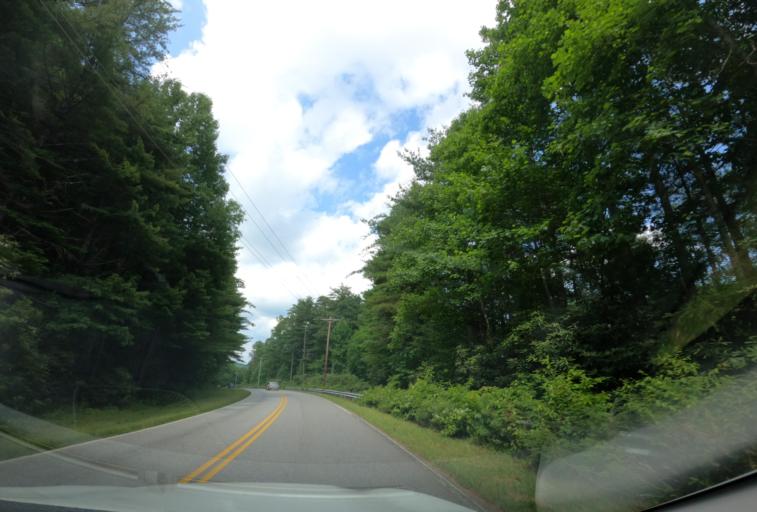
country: US
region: North Carolina
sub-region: Jackson County
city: Cullowhee
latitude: 35.0694
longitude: -83.0056
